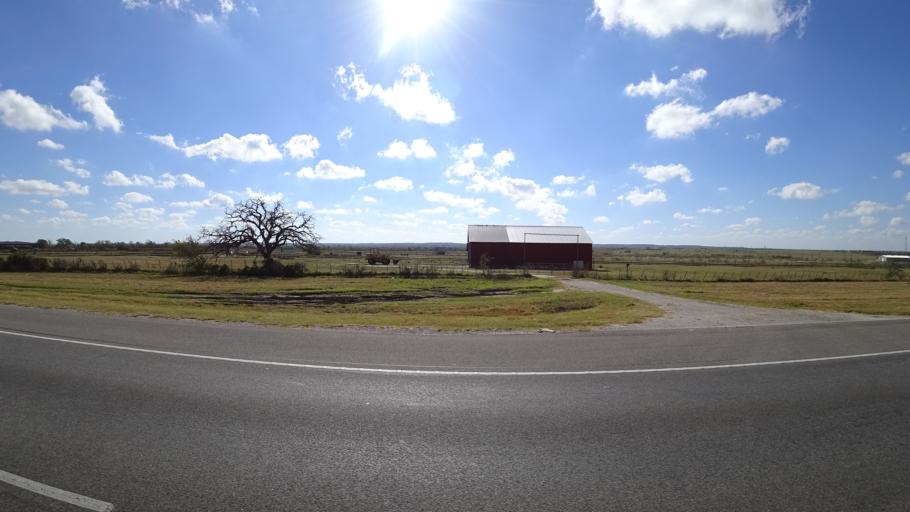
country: US
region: Texas
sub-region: Travis County
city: Garfield
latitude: 30.1885
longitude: -97.5885
